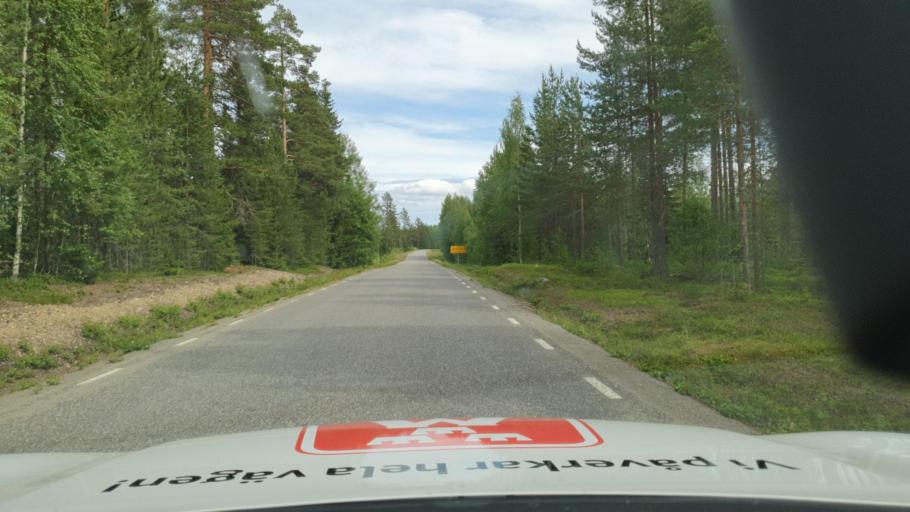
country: SE
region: Vaesterbotten
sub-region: Skelleftea Kommun
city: Viken
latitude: 64.4980
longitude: 20.8899
